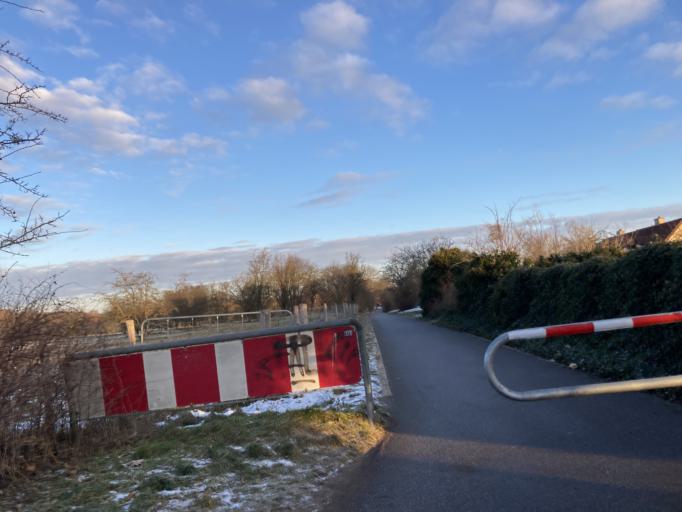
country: DK
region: Capital Region
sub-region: Gladsaxe Municipality
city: Buddinge
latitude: 55.7678
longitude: 12.4761
